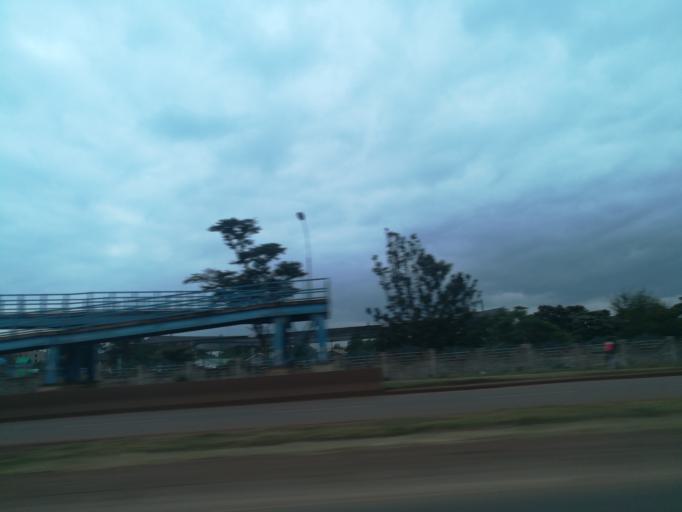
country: KE
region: Nairobi Area
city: Thika
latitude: -1.1214
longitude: 37.0073
